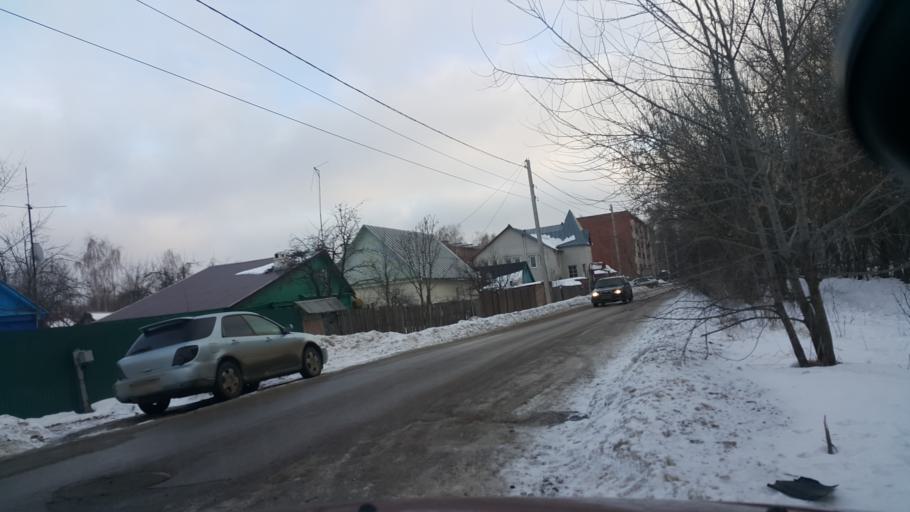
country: RU
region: Tambov
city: Kotovsk
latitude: 52.6010
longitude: 41.5011
